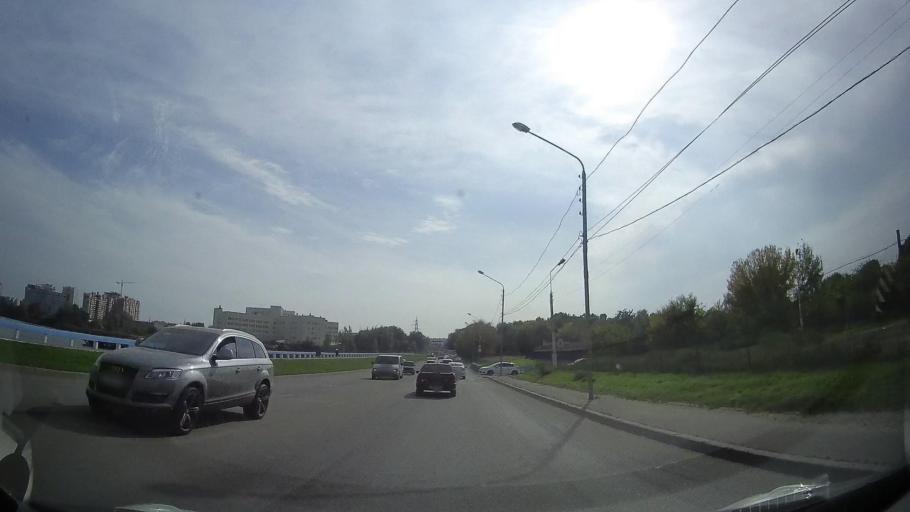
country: RU
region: Rostov
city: Severnyy
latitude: 47.2778
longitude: 39.7045
